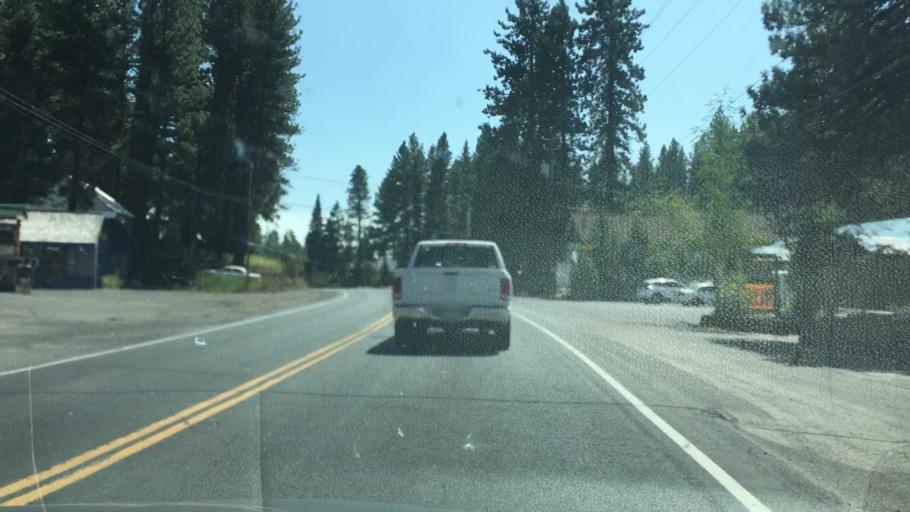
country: US
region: Idaho
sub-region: Valley County
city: McCall
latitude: 44.9041
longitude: -116.0982
